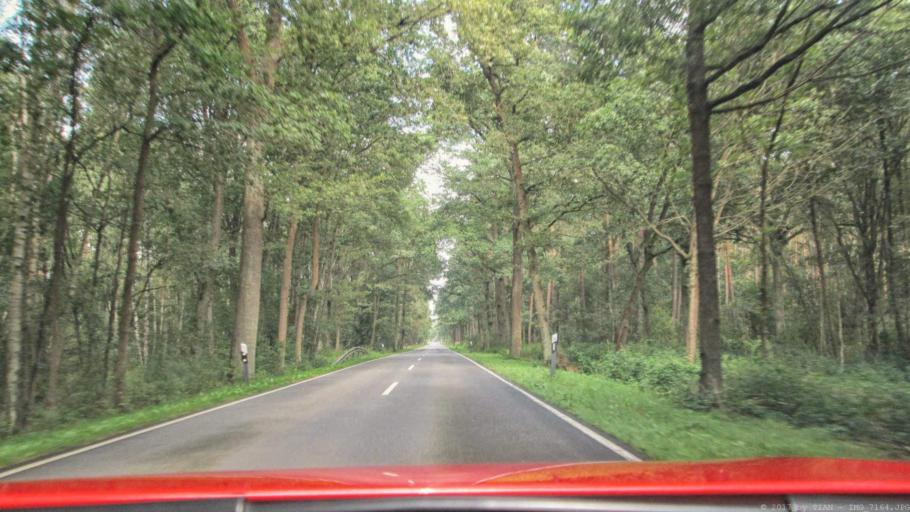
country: DE
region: Lower Saxony
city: Neetze
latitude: 53.2840
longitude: 10.6438
